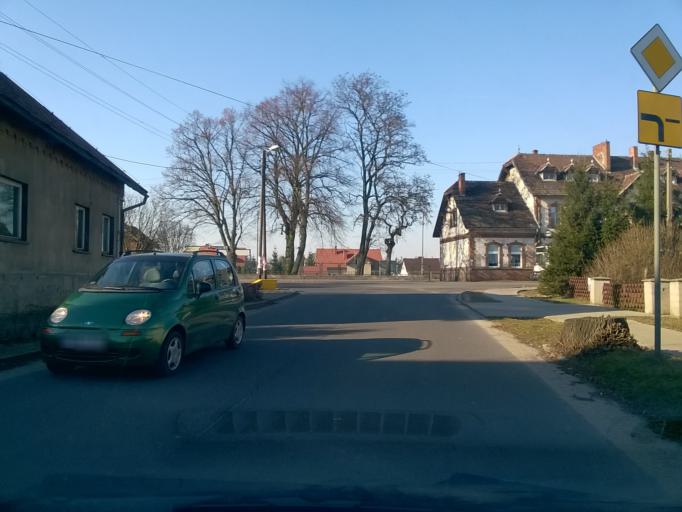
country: PL
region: Greater Poland Voivodeship
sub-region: Powiat wagrowiecki
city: Golancz
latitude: 52.9468
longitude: 17.3059
